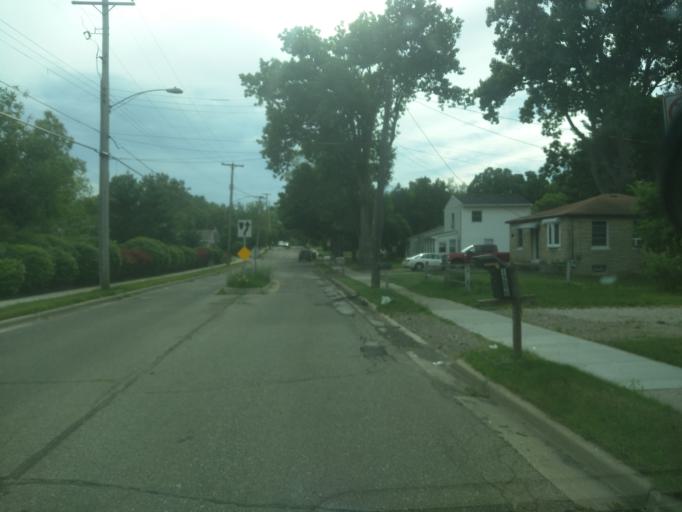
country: US
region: Michigan
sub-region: Ingham County
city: Lansing
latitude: 42.6912
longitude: -84.5691
